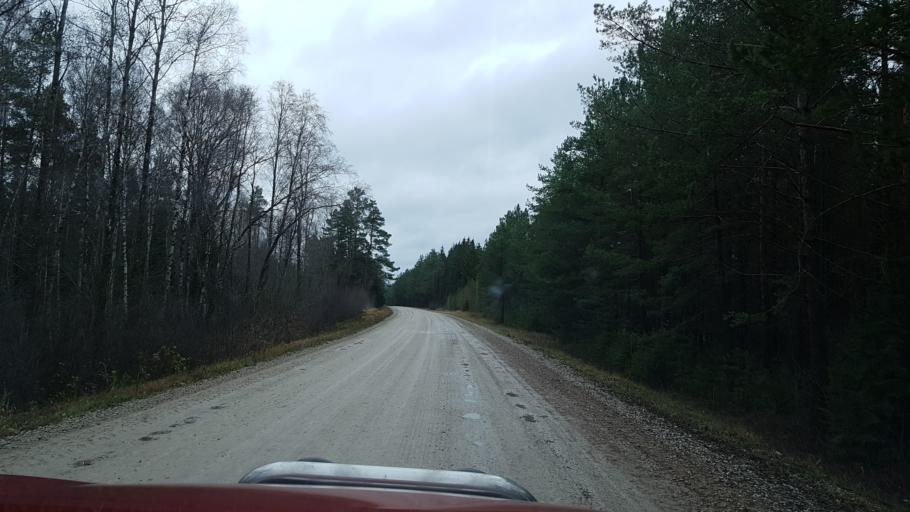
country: EE
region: Paernumaa
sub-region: Halinga vald
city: Parnu-Jaagupi
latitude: 58.5526
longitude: 24.4120
